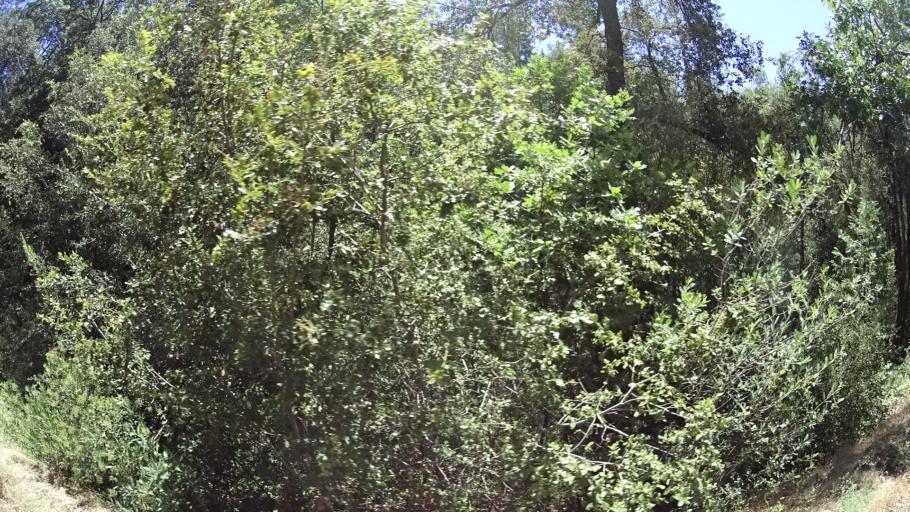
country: US
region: California
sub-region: Calaveras County
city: Forest Meadows
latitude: 38.1412
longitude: -120.4187
